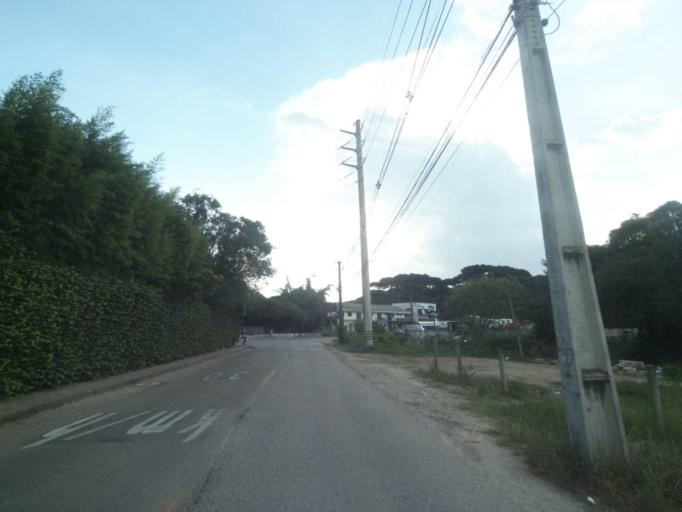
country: BR
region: Parana
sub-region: Sao Jose Dos Pinhais
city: Sao Jose dos Pinhais
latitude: -25.5357
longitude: -49.2837
